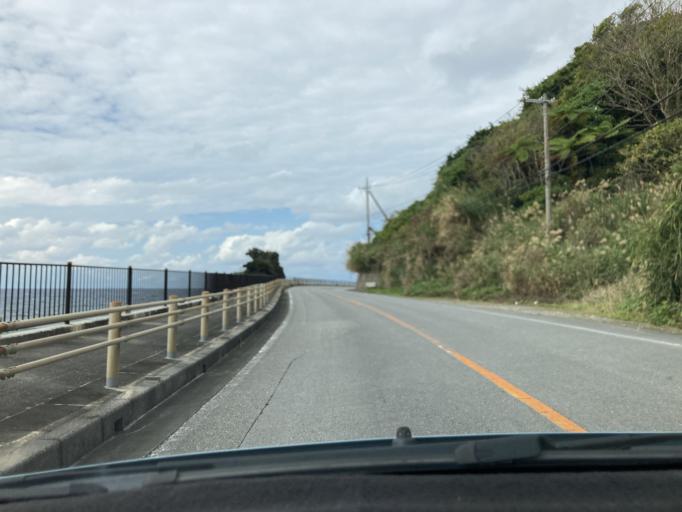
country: JP
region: Okinawa
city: Nago
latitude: 26.8004
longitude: 128.2323
